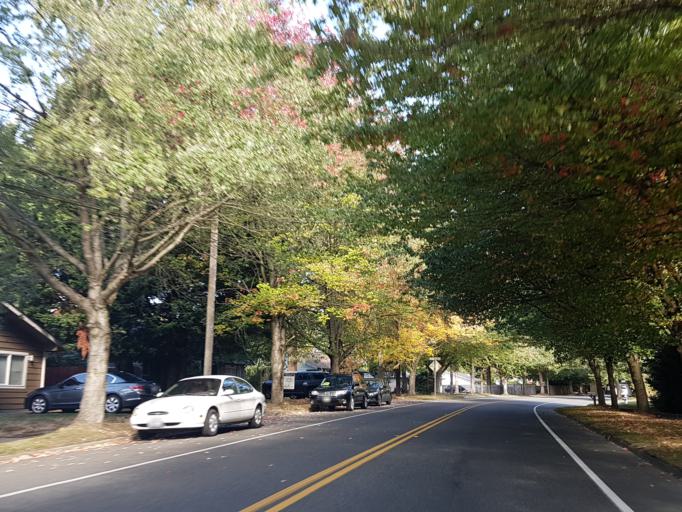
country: US
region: Washington
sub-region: Snohomish County
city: Brier
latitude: 47.7689
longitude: -122.2642
